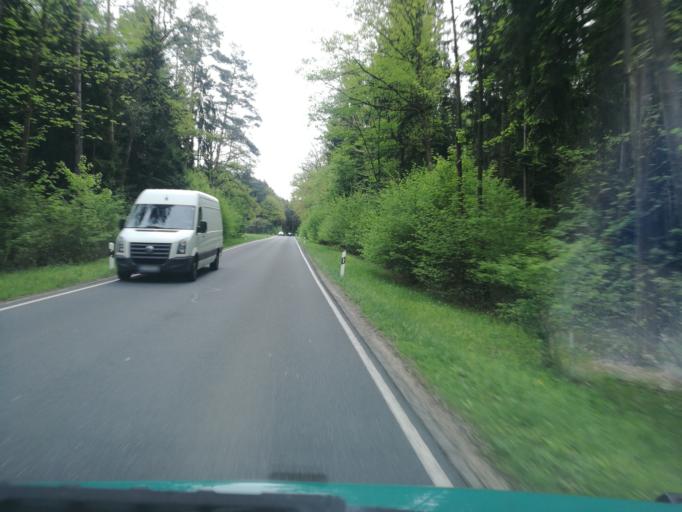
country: DE
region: Bavaria
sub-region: Upper Franconia
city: Sonnefeld
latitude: 50.2017
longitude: 11.1080
